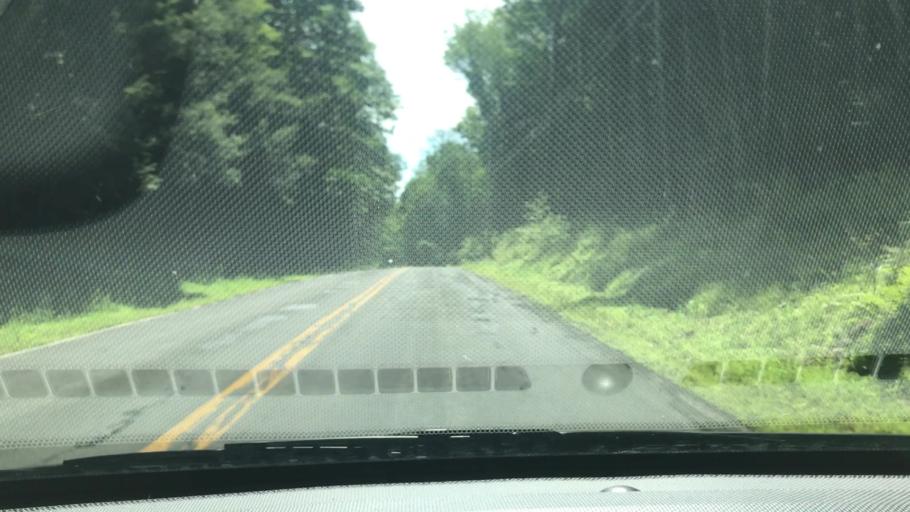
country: US
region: New York
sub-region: Ulster County
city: Shokan
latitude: 41.9510
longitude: -74.2593
